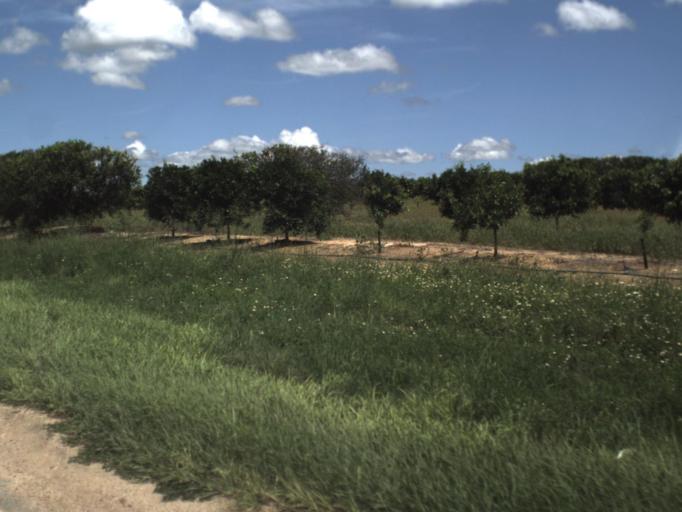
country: US
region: Florida
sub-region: Polk County
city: Dundee
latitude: 27.9937
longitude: -81.5949
